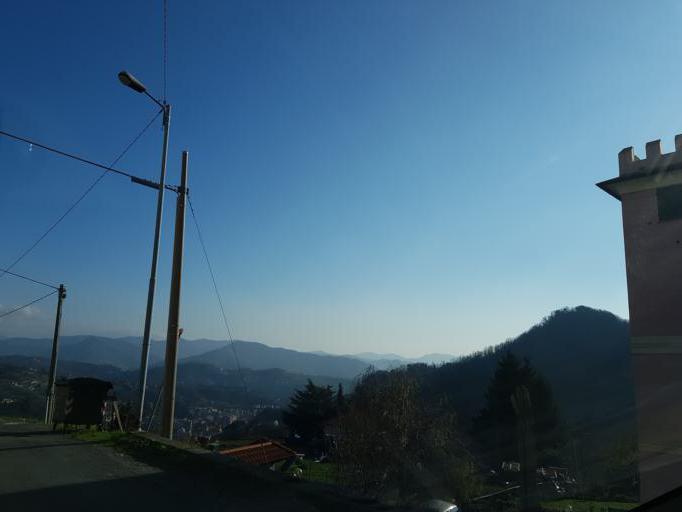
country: IT
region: Liguria
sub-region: Provincia di Genova
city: Campomorone
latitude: 44.5082
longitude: 8.8745
